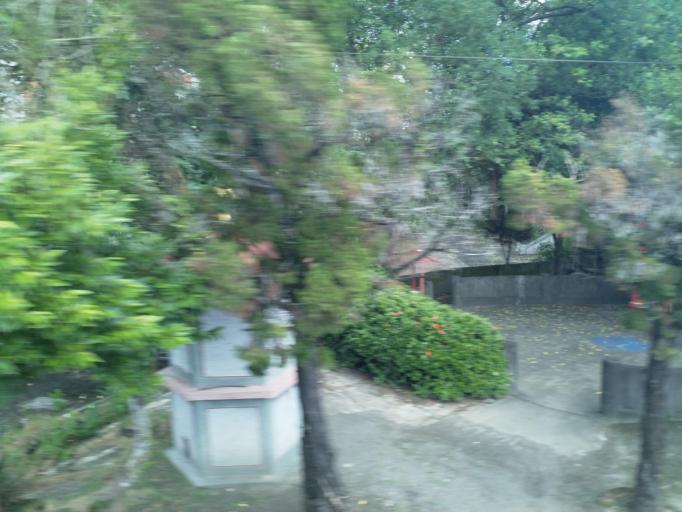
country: TW
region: Taiwan
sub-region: Pingtung
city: Pingtung
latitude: 22.8885
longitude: 120.5511
